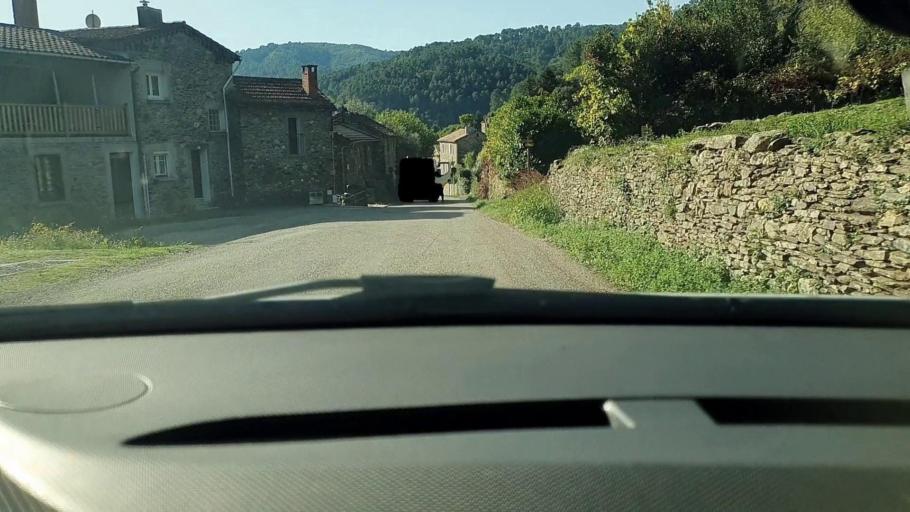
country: FR
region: Languedoc-Roussillon
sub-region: Departement du Gard
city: Besseges
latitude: 44.3090
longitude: 4.0598
